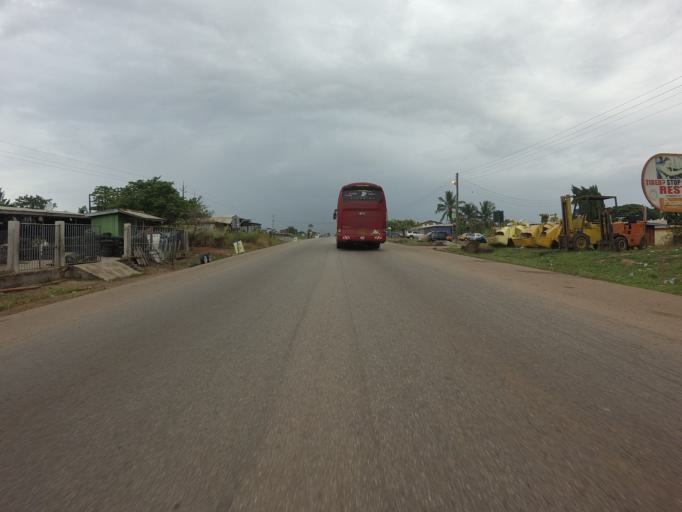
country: GH
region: Ashanti
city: Konongo
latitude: 6.6192
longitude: -1.1925
